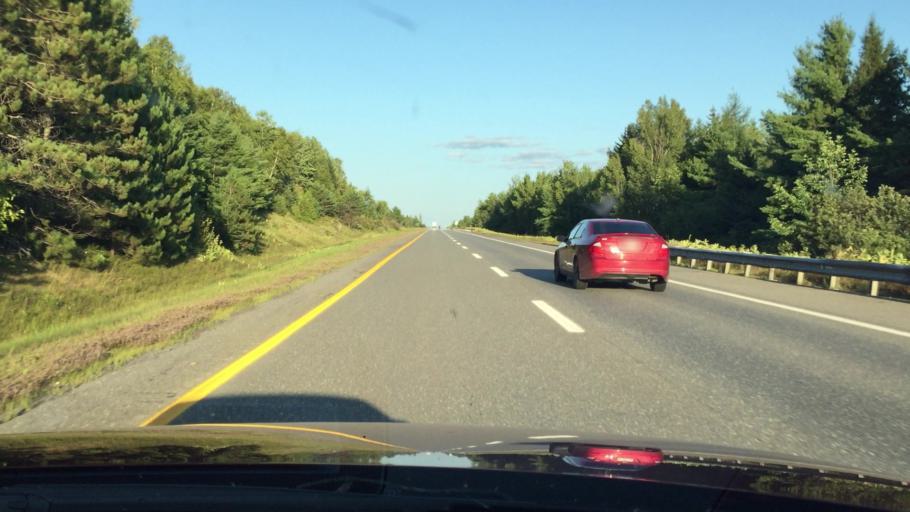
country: US
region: Maine
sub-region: Aroostook County
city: Hodgdon
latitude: 46.1446
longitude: -68.0516
